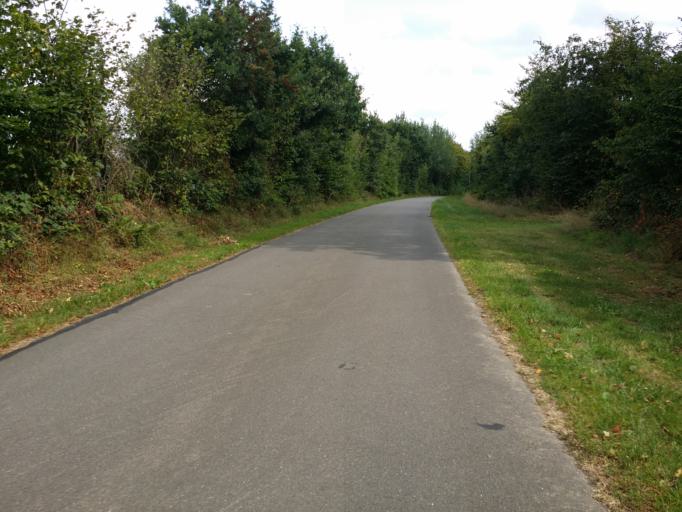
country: DE
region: Schleswig-Holstein
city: Mehlbek
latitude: 54.0022
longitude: 9.4271
